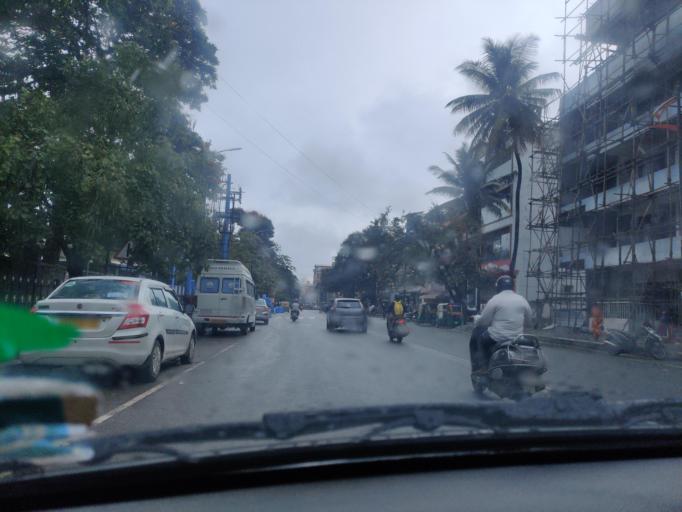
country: IN
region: Karnataka
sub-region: Bangalore Urban
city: Bangalore
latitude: 13.0186
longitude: 77.6367
